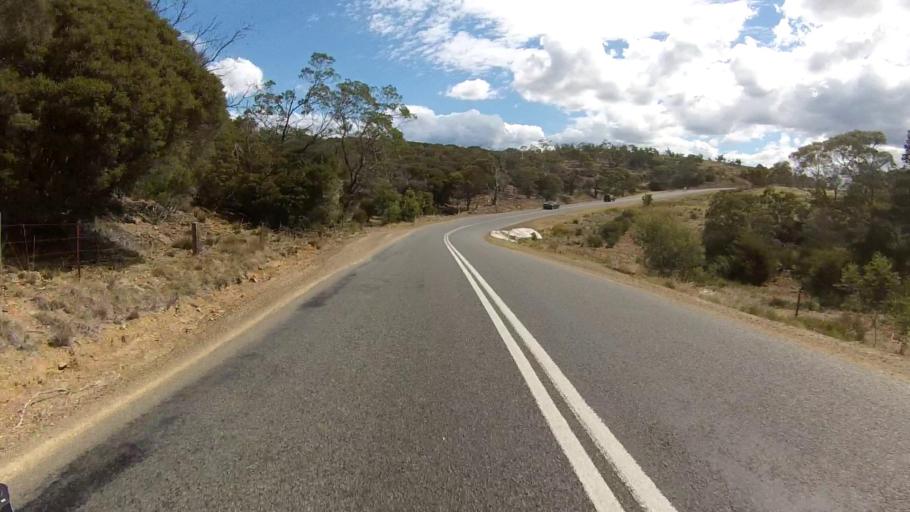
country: AU
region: Tasmania
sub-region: Break O'Day
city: St Helens
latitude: -41.9944
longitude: 148.1081
